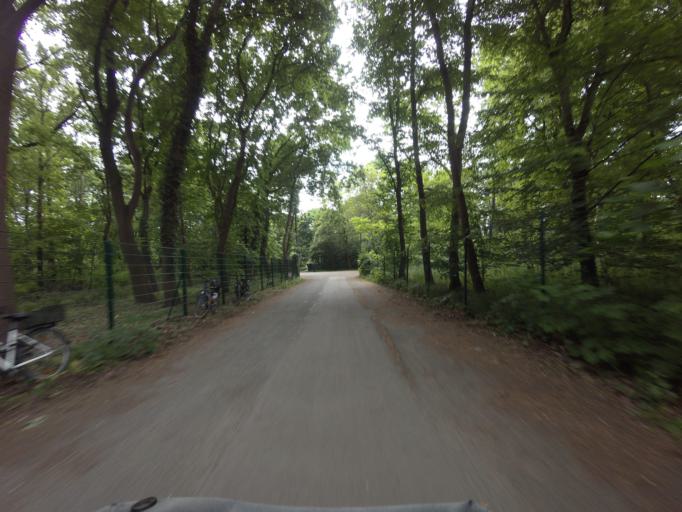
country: DE
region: Lower Saxony
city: Braunschweig
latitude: 52.2918
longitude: 10.5336
